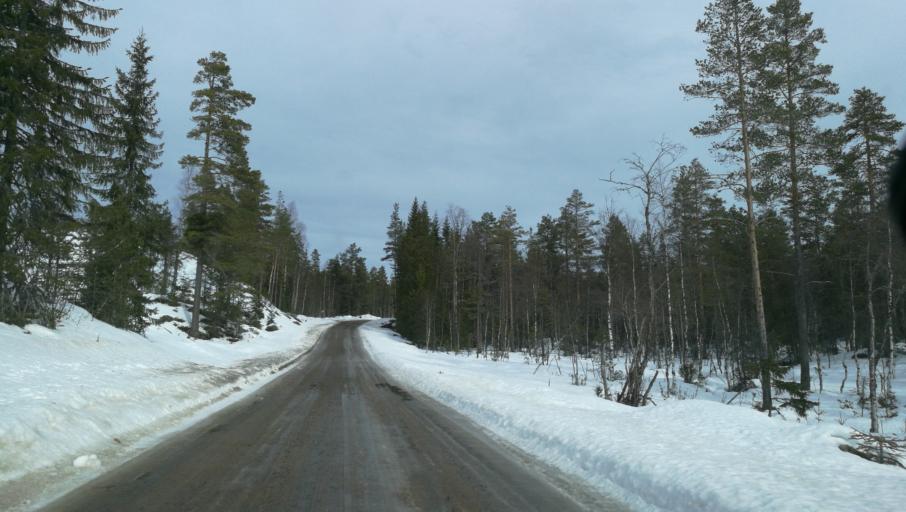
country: SE
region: Vaermland
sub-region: Torsby Kommun
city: Torsby
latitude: 60.6438
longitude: 12.7984
